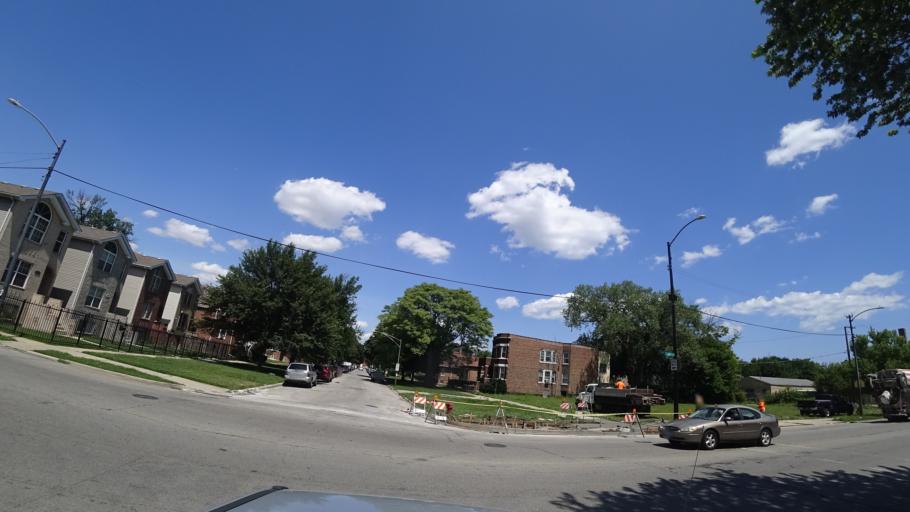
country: US
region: Illinois
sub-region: Cook County
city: Chicago
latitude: 41.7692
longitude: -87.6218
